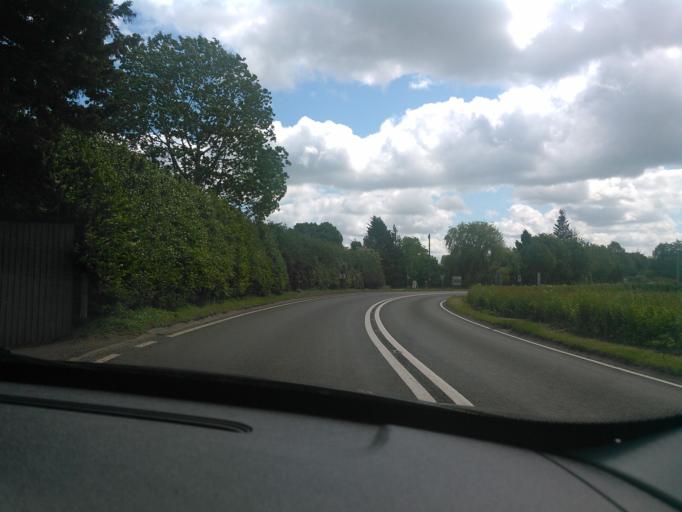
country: GB
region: England
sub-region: Shropshire
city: Prees
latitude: 52.8816
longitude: -2.6569
